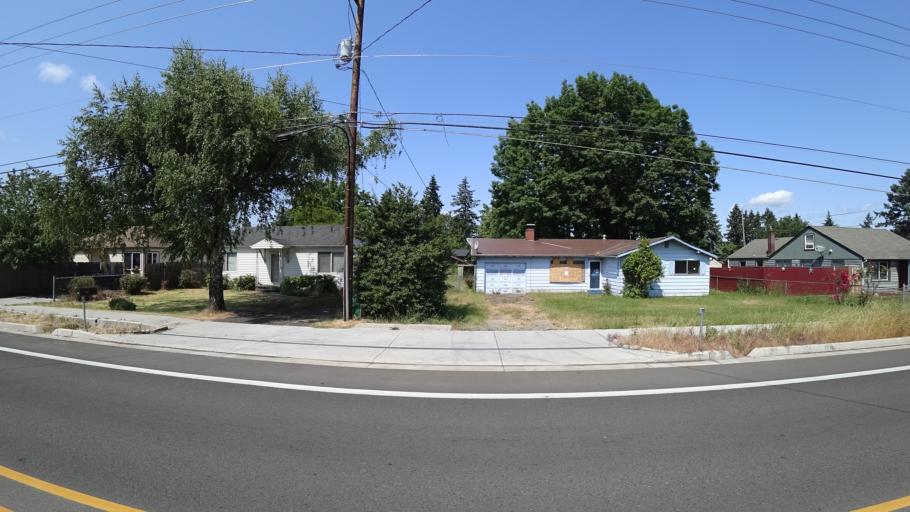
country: US
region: Oregon
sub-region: Multnomah County
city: Lents
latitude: 45.4522
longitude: -122.5929
